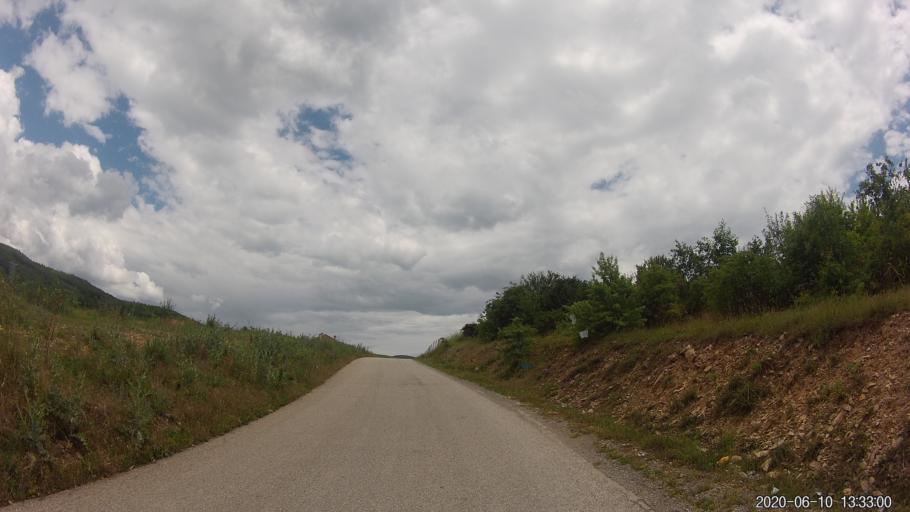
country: XK
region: Prizren
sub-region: Komuna e Therandes
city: Budakovo
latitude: 42.4106
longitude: 20.8851
